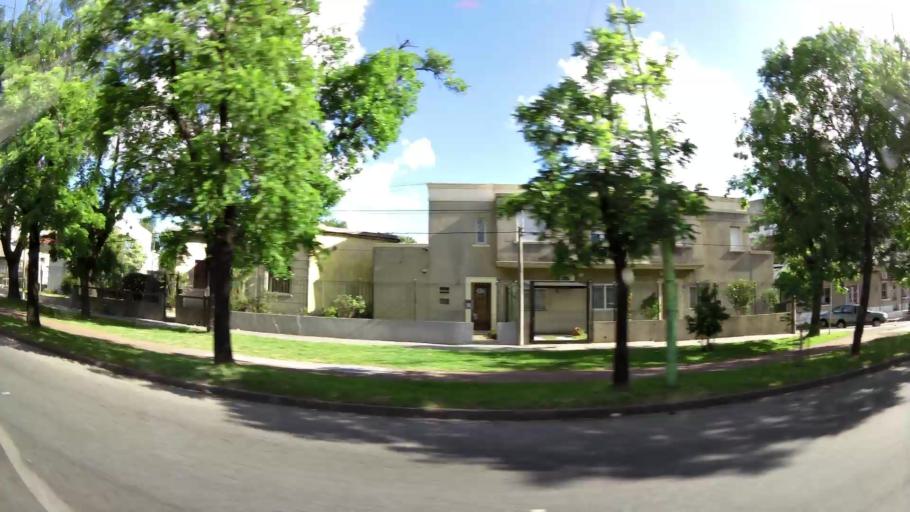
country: UY
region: Montevideo
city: Montevideo
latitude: -34.8716
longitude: -56.1920
